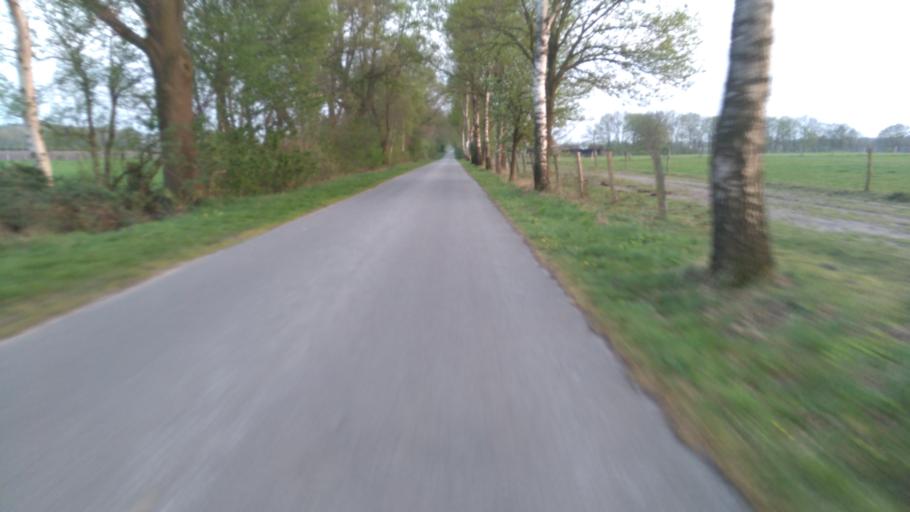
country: DE
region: Lower Saxony
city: Bargstedt
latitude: 53.4842
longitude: 9.4784
